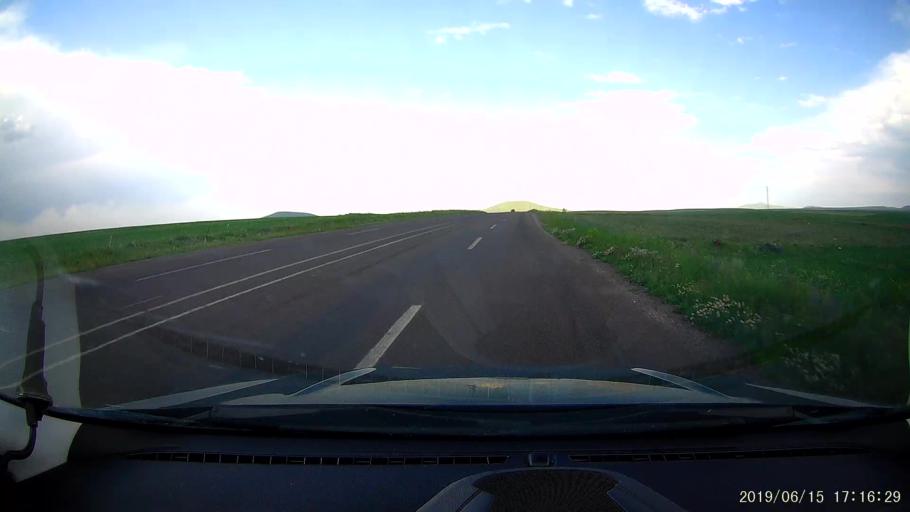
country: TR
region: Kars
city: Kars
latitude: 40.6147
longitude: 43.2186
